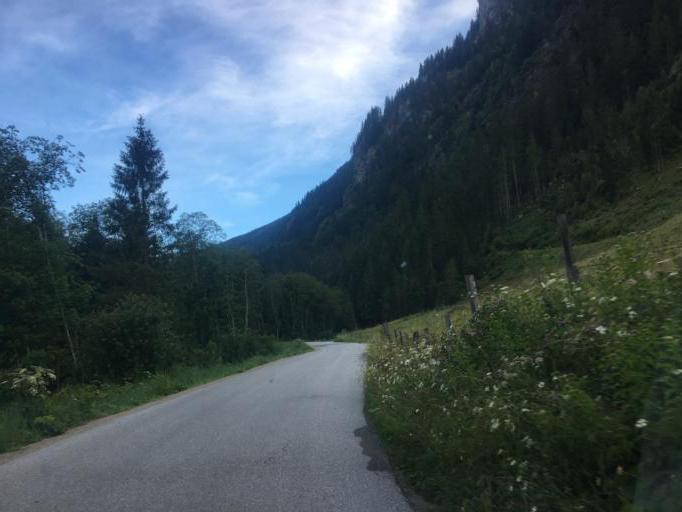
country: AT
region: Styria
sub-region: Politischer Bezirk Liezen
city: Haus
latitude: 47.3379
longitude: 13.7426
